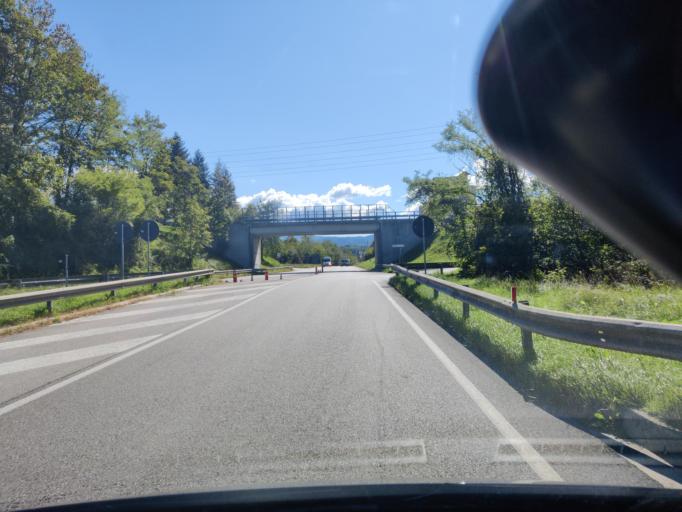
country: IT
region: Veneto
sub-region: Provincia di Belluno
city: Soccher-Paiane-Casan-Arsie
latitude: 46.1648
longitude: 12.3153
